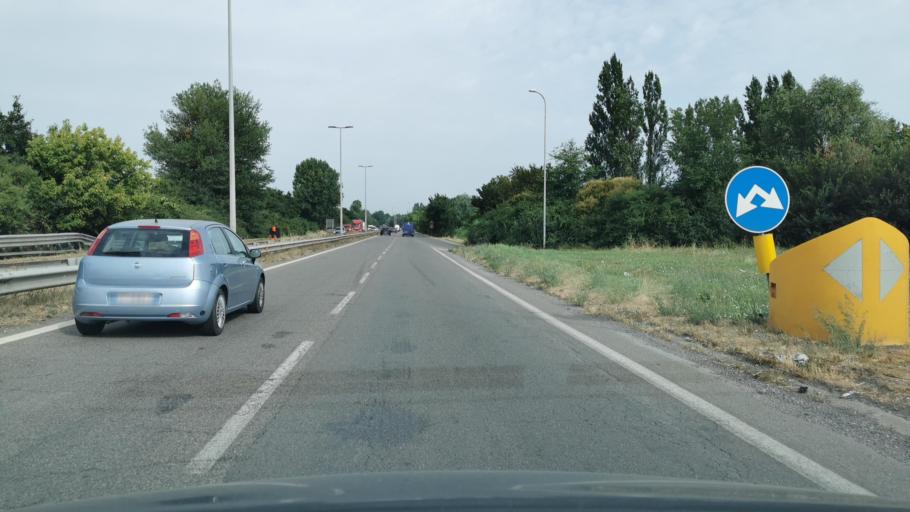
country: IT
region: Emilia-Romagna
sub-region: Provincia di Modena
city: Modena
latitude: 44.6654
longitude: 10.9361
